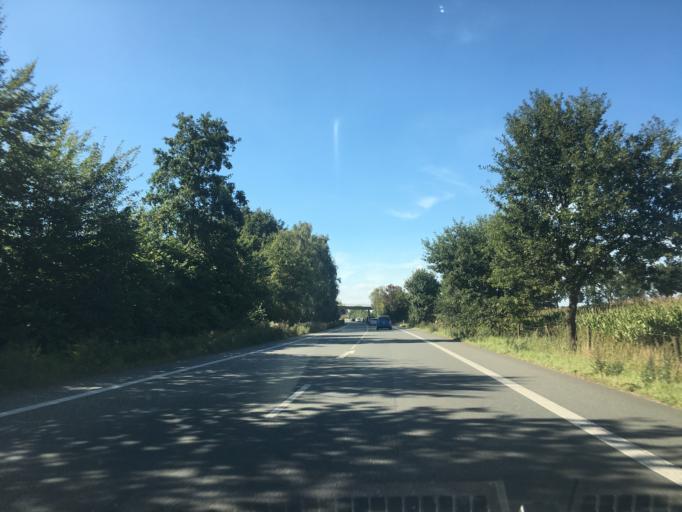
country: DE
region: North Rhine-Westphalia
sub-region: Regierungsbezirk Detmold
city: Rheda-Wiedenbruck
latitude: 51.8788
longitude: 8.2984
